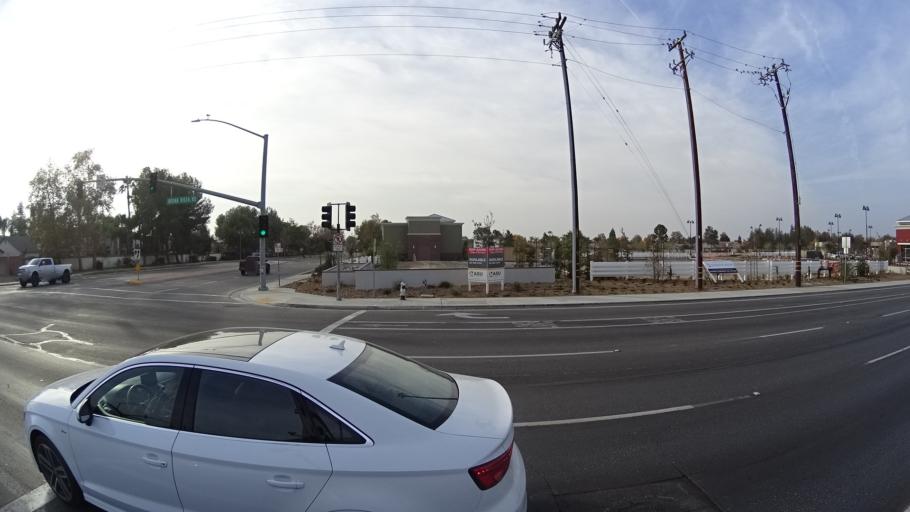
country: US
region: California
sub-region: Kern County
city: Greenacres
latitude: 35.3471
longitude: -119.1278
